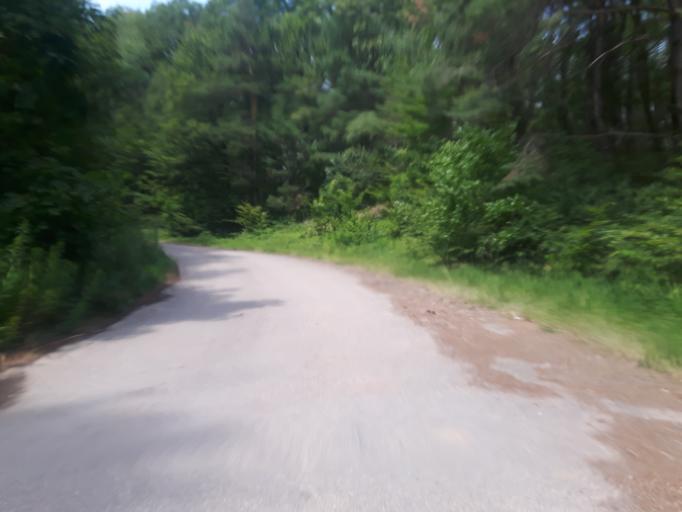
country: DE
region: Baden-Wuerttemberg
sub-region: Regierungsbezirk Stuttgart
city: Pfaffenhofen
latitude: 49.0388
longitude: 8.9835
